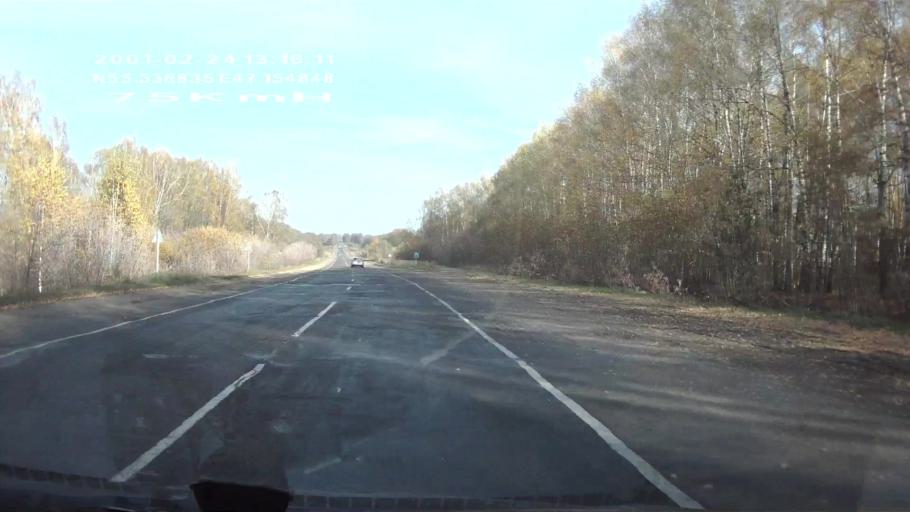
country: RU
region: Chuvashia
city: Ibresi
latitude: 55.3368
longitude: 47.1551
